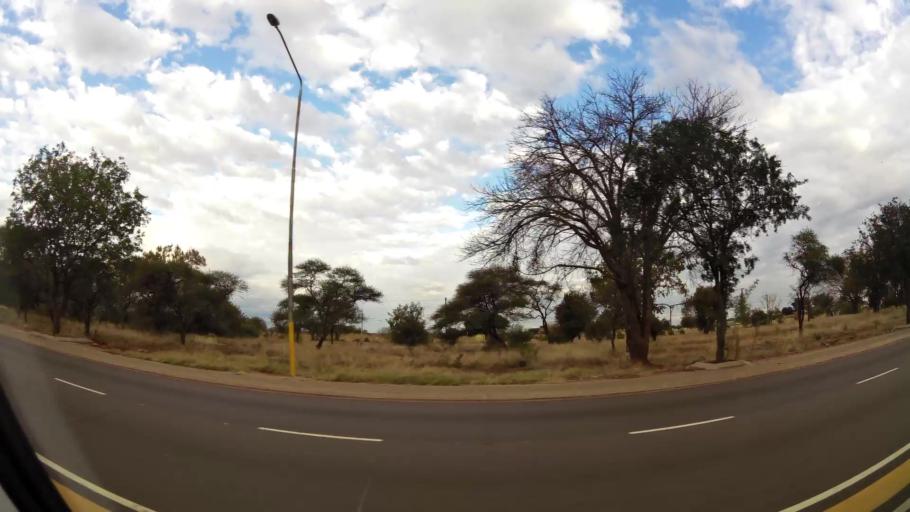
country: ZA
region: Limpopo
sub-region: Waterberg District Municipality
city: Modimolle
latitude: -24.5119
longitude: 28.7221
